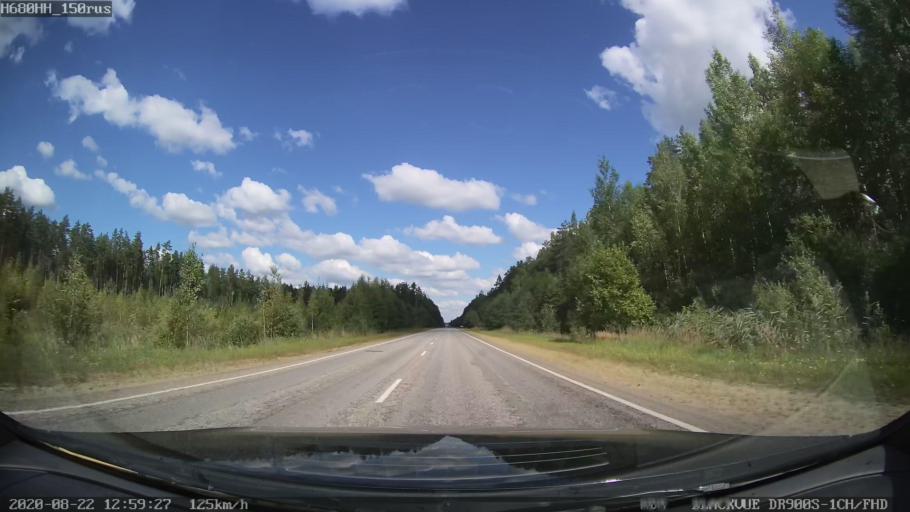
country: RU
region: Tverskaya
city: Bezhetsk
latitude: 57.6061
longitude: 36.3599
